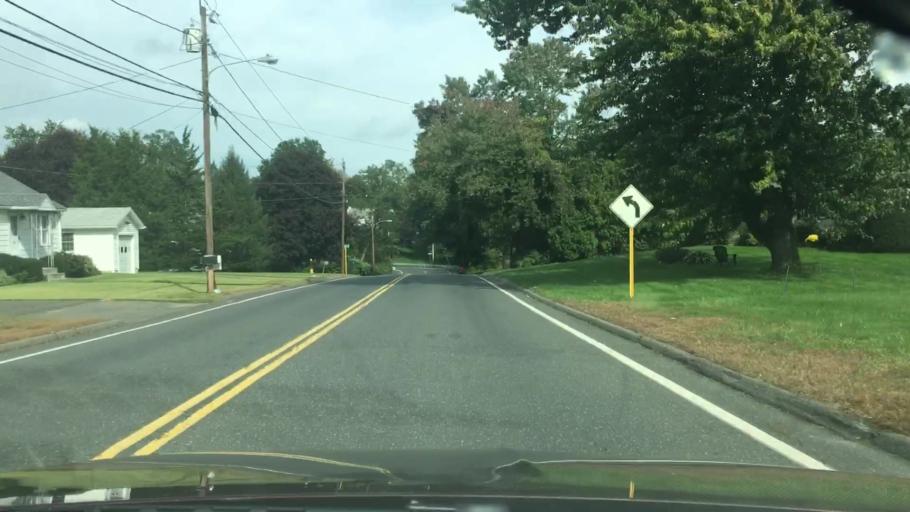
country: US
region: Massachusetts
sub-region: Hampden County
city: East Longmeadow
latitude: 42.0742
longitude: -72.5305
